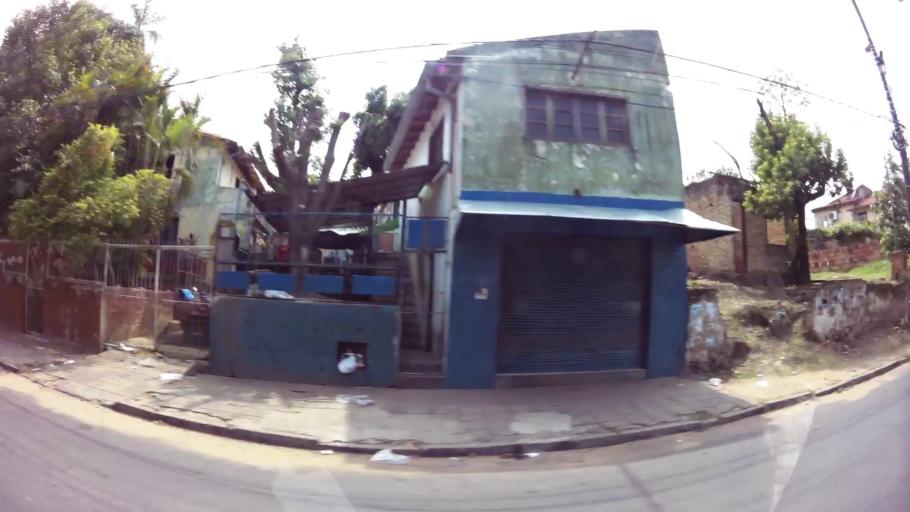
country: PY
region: Asuncion
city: Asuncion
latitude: -25.2604
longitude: -57.5815
